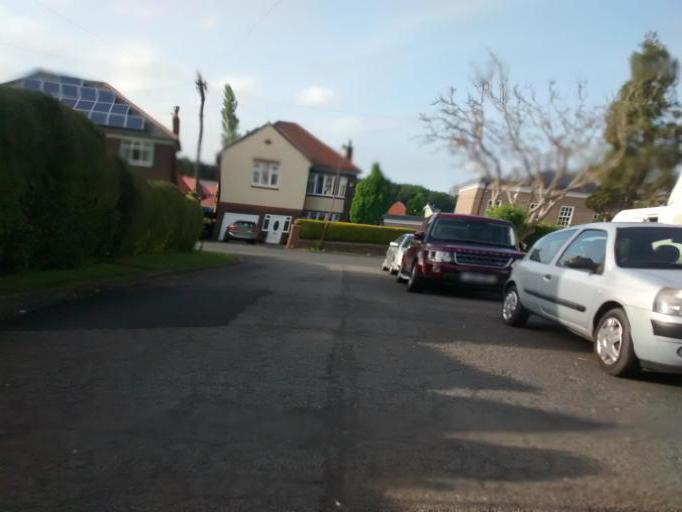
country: GB
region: England
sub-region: County Durham
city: Durham
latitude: 54.7559
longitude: -1.5890
